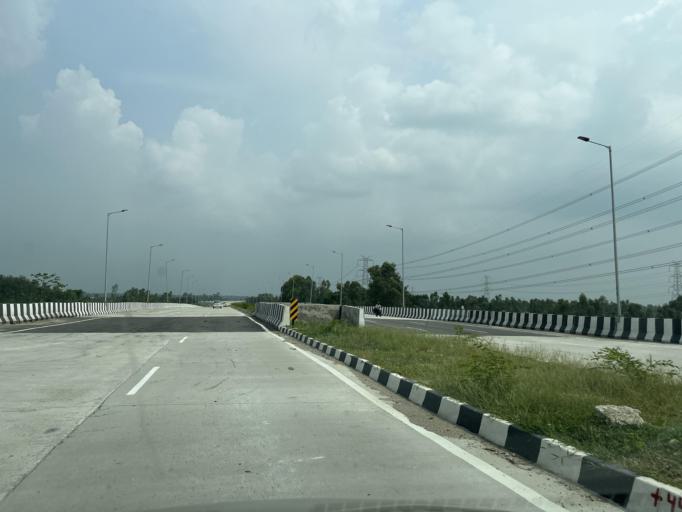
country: IN
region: Uttarakhand
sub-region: Udham Singh Nagar
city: Jaspur
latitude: 29.2949
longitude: 78.8426
